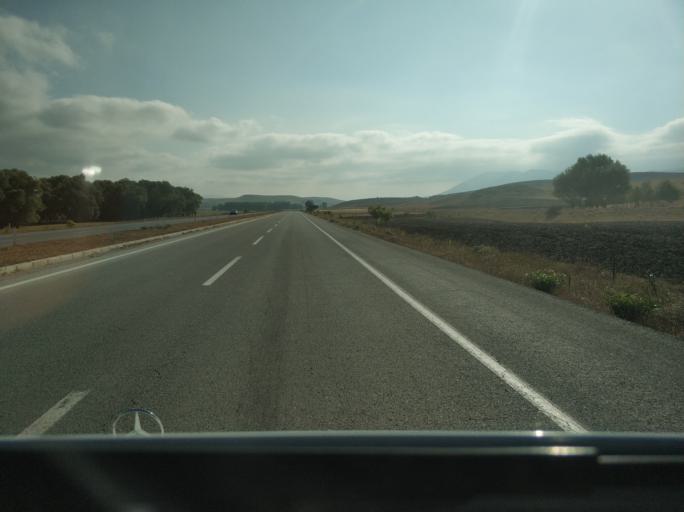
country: TR
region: Sivas
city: Yildizeli
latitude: 39.8477
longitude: 36.4886
